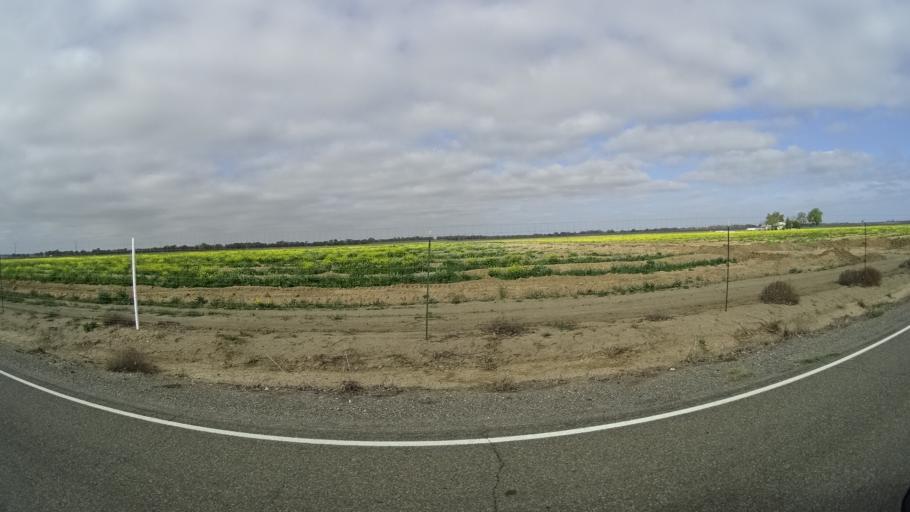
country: US
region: California
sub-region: Colusa County
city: Colusa
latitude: 39.4124
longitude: -121.9665
